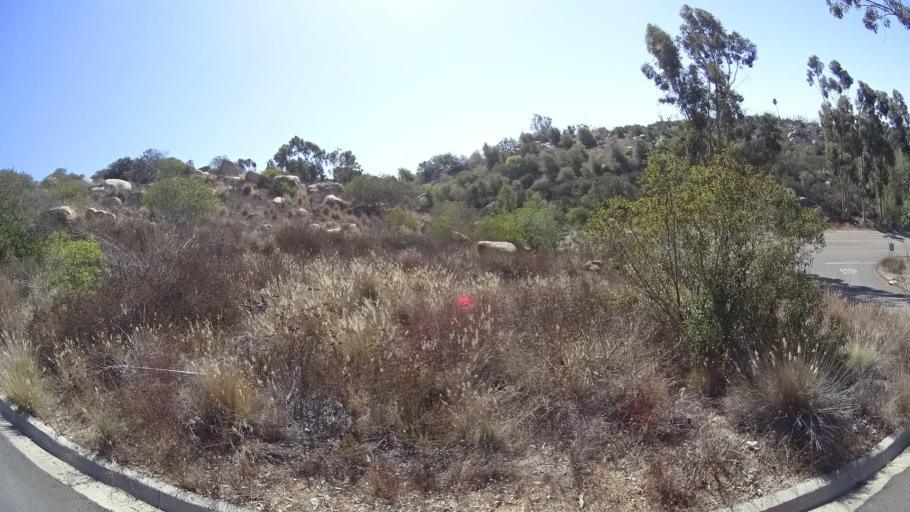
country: US
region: California
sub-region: San Diego County
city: Hidden Meadows
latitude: 33.2039
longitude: -117.1163
